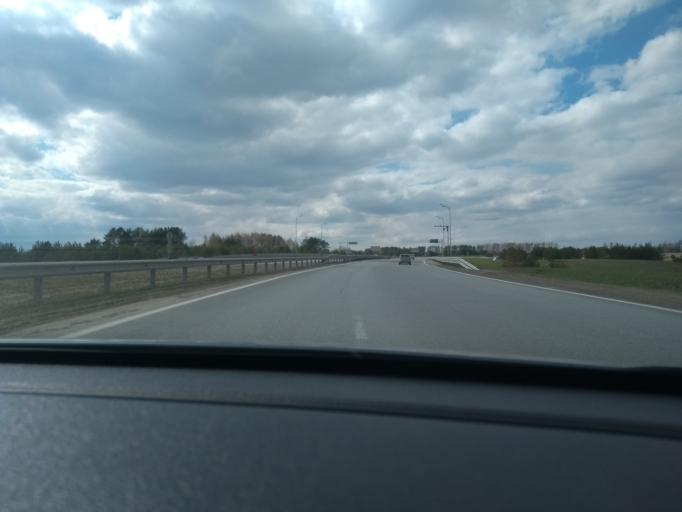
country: RU
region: Tatarstan
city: Yelabuga
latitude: 55.7817
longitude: 52.1788
